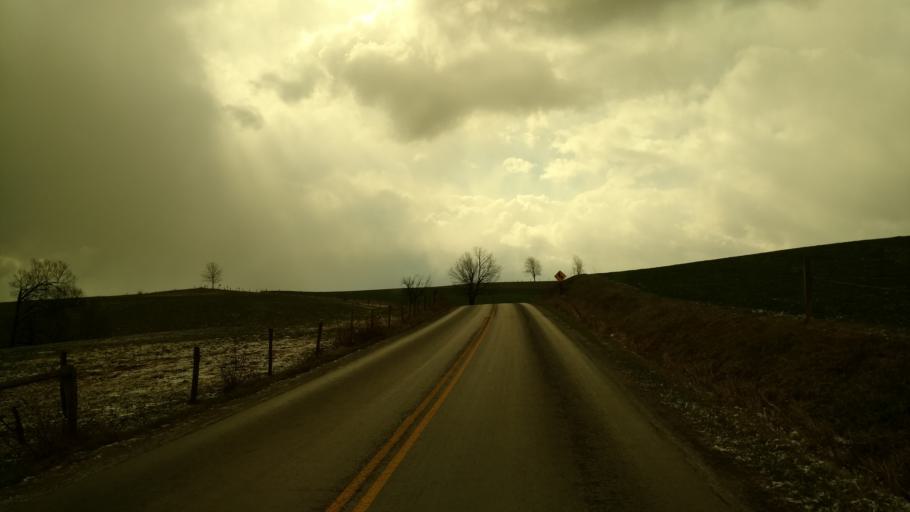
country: US
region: Ohio
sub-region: Tuscarawas County
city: Sugarcreek
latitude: 40.4663
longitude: -81.7779
